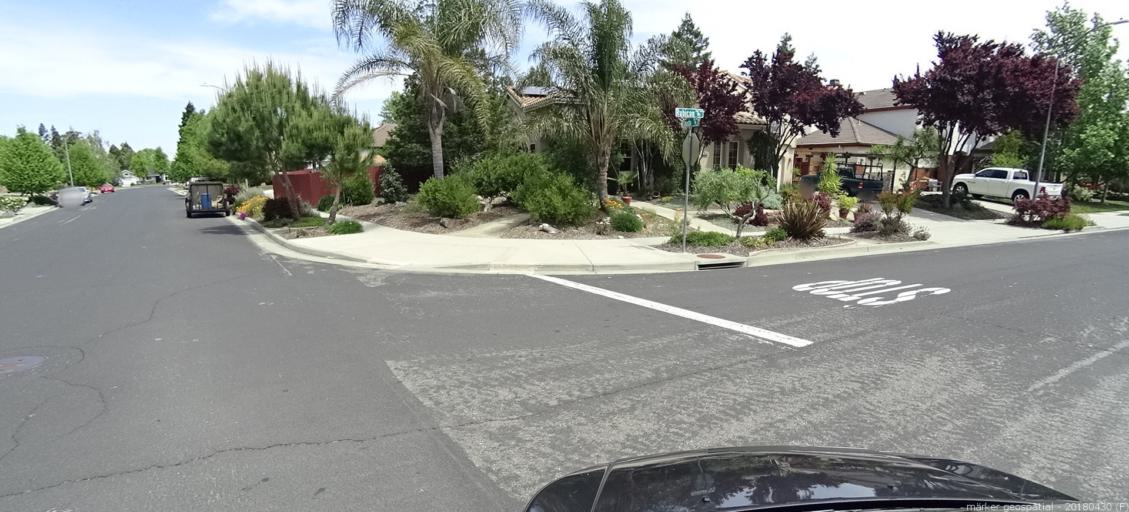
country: US
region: California
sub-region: Yolo County
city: West Sacramento
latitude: 38.5438
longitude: -121.5317
